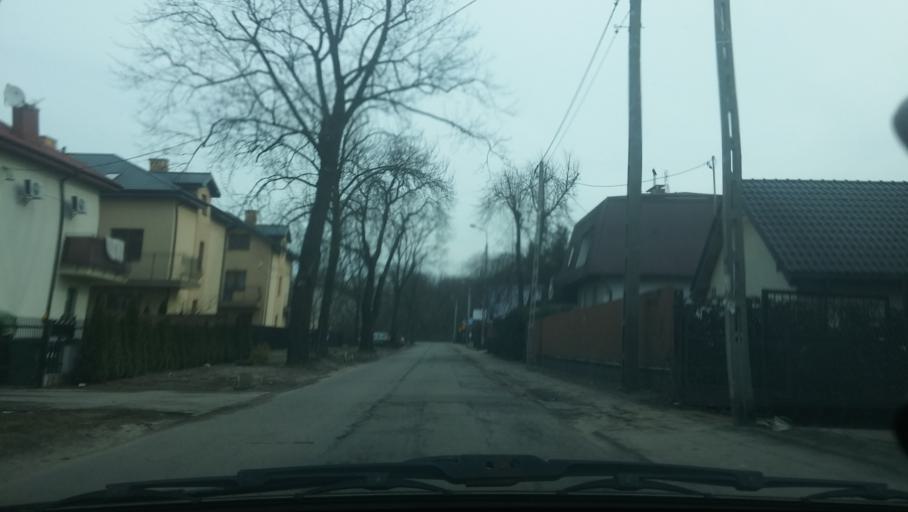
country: PL
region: Masovian Voivodeship
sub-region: Powiat wolominski
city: Zabki
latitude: 52.3047
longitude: 21.1032
